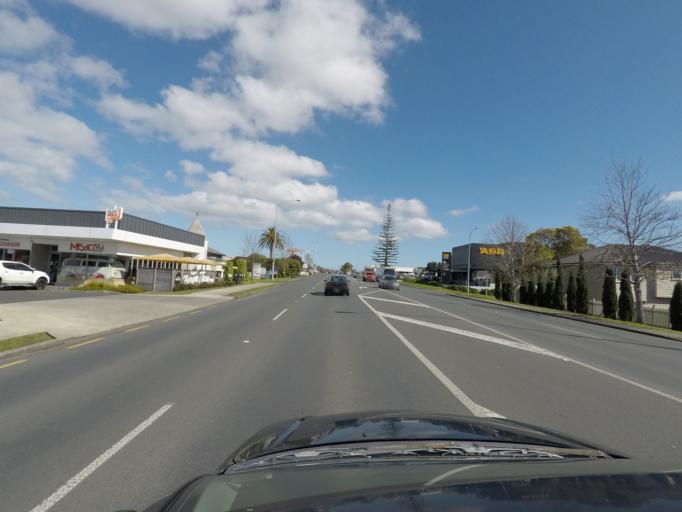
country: NZ
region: Auckland
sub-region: Auckland
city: Rosebank
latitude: -36.8532
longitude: 174.6301
